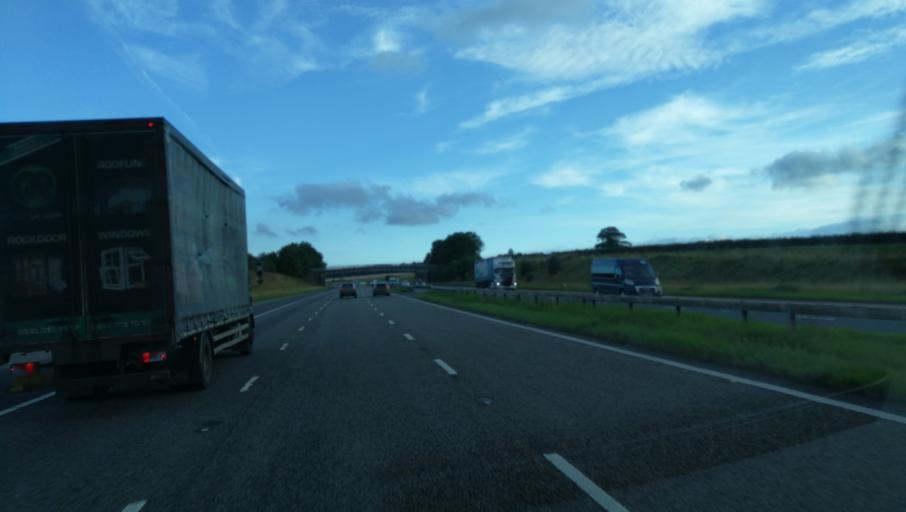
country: GB
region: England
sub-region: Cumbria
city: Penrith
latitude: 54.6255
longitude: -2.7226
